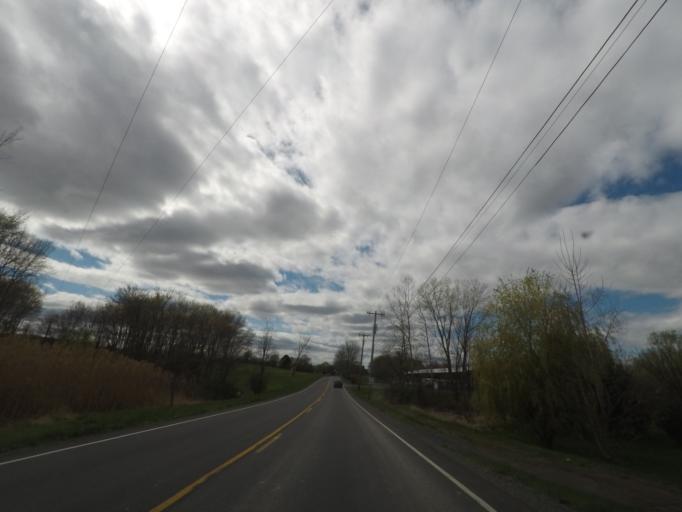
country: US
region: New York
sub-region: Columbia County
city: Valatie
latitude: 42.3955
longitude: -73.6462
